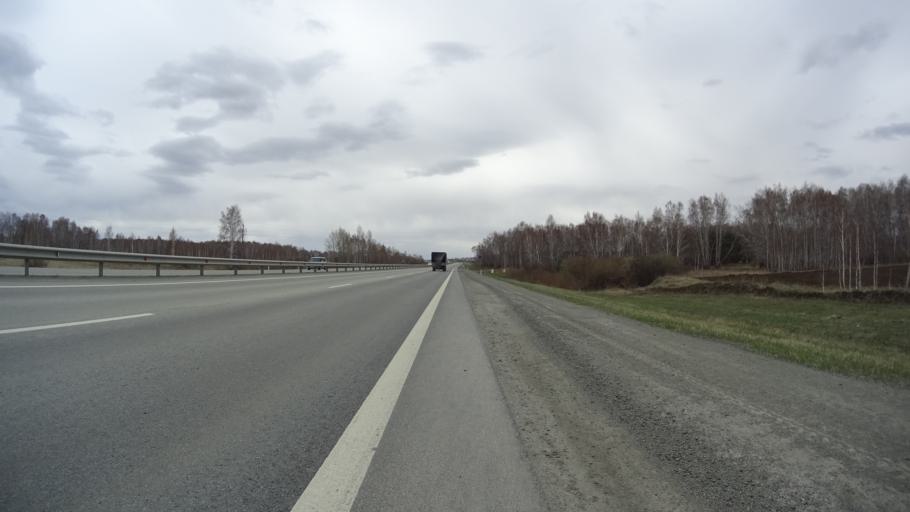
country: RU
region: Chelyabinsk
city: Yemanzhelinka
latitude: 54.8289
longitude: 61.3110
